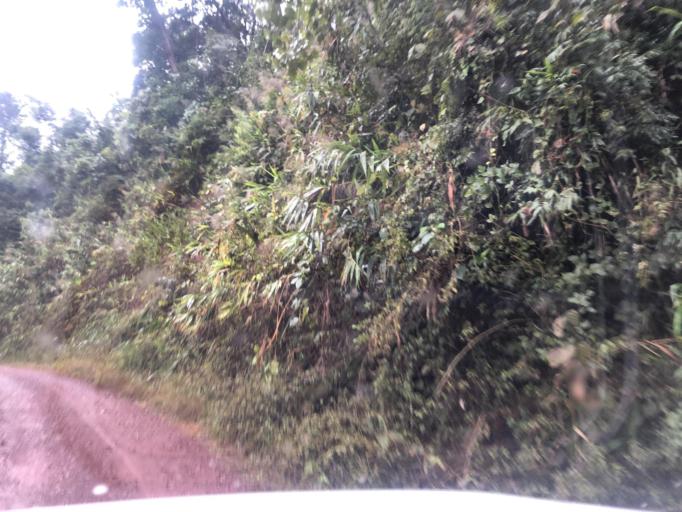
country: LA
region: Oudomxai
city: Muang La
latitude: 21.2451
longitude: 101.9383
